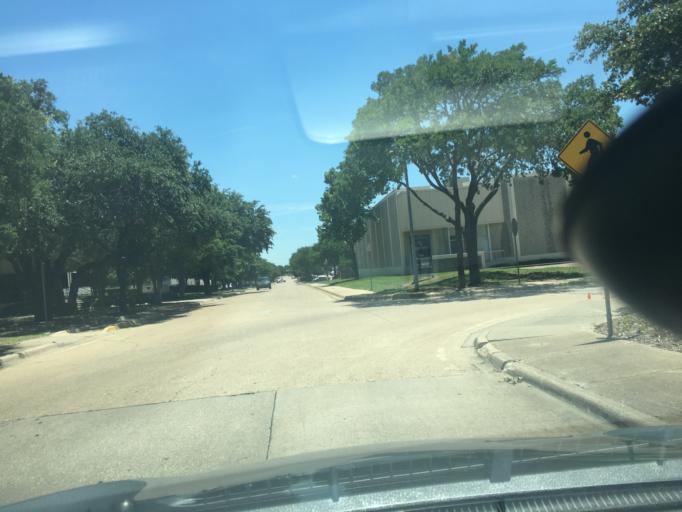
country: US
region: Texas
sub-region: Dallas County
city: Richardson
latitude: 32.9643
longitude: -96.7093
